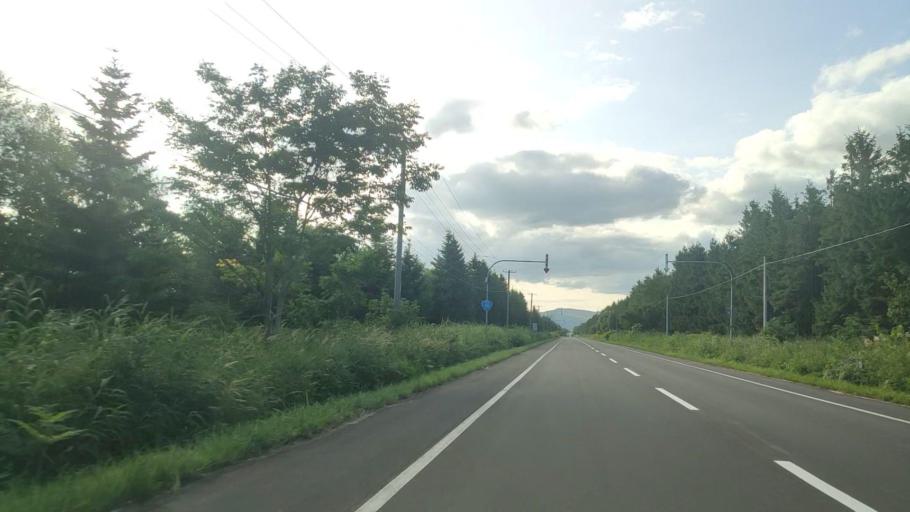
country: JP
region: Hokkaido
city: Makubetsu
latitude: 44.8852
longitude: 142.0117
